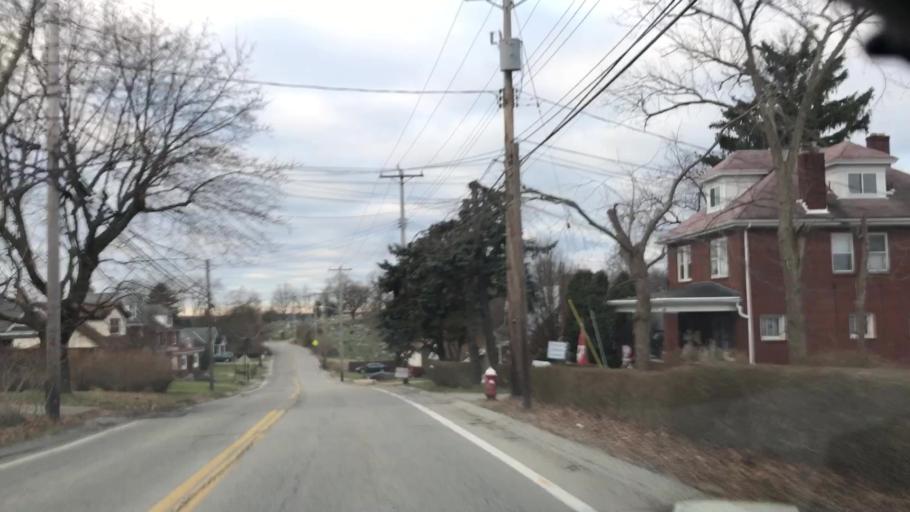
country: US
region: Pennsylvania
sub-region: Allegheny County
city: West View
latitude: 40.5130
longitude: -80.0335
